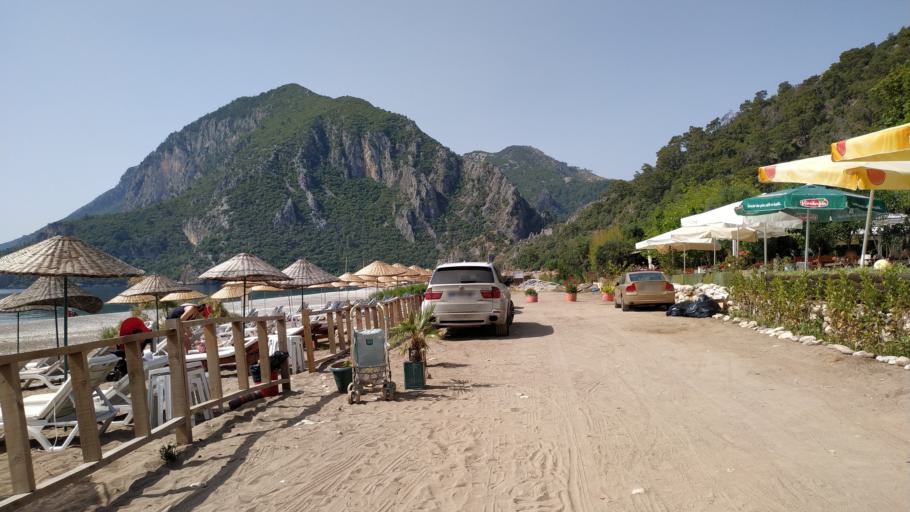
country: TR
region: Antalya
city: Tekirova
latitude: 36.4026
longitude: 30.4769
